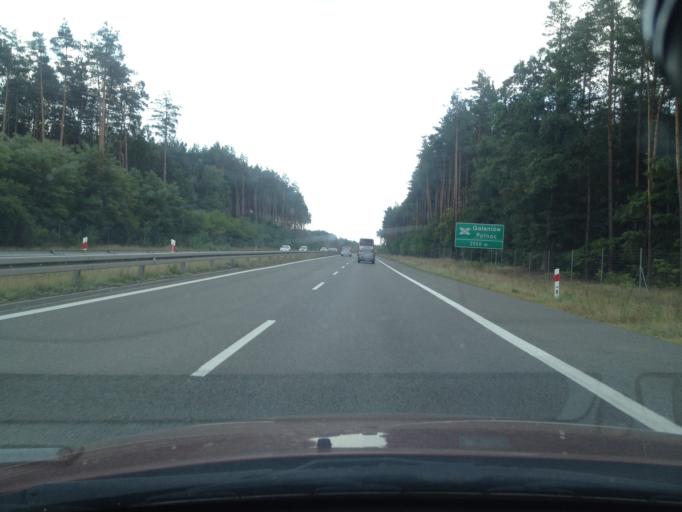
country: PL
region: West Pomeranian Voivodeship
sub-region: Powiat goleniowski
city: Goleniow
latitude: 53.6115
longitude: 14.8186
